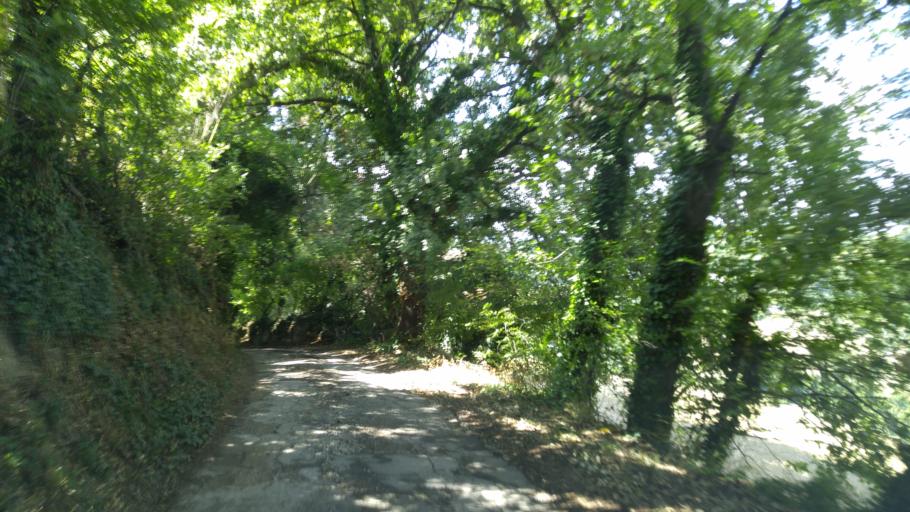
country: IT
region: The Marches
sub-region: Provincia di Pesaro e Urbino
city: Centinarola
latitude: 43.8135
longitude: 12.9729
